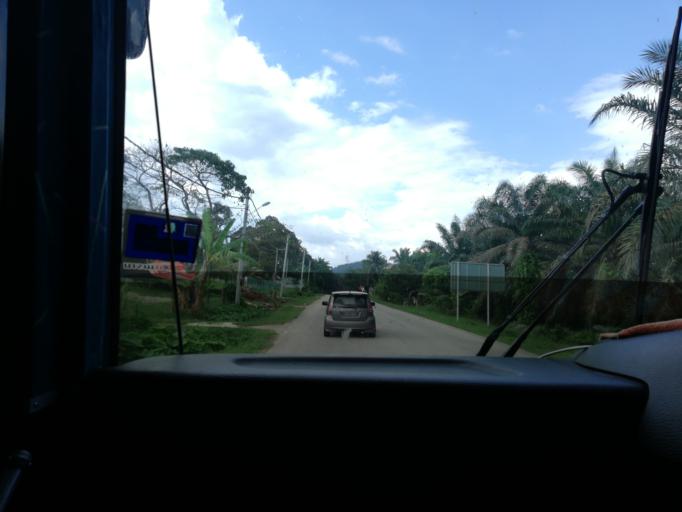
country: MY
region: Kedah
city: Kulim
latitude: 5.2590
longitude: 100.6053
